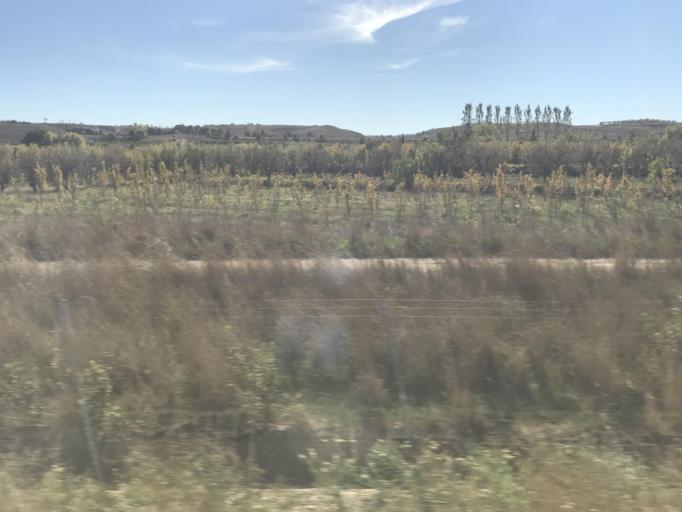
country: ES
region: Aragon
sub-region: Provincia de Zaragoza
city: Terrer
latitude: 41.3253
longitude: -1.6921
